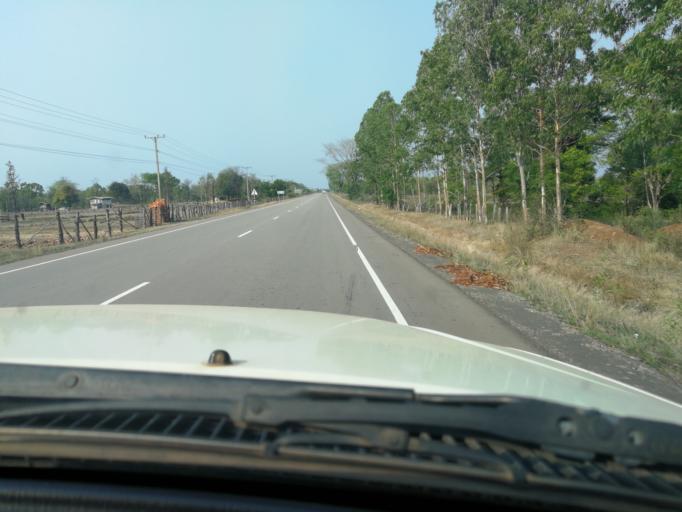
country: TH
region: Mukdahan
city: Wan Yai
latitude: 16.7110
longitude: 105.2425
